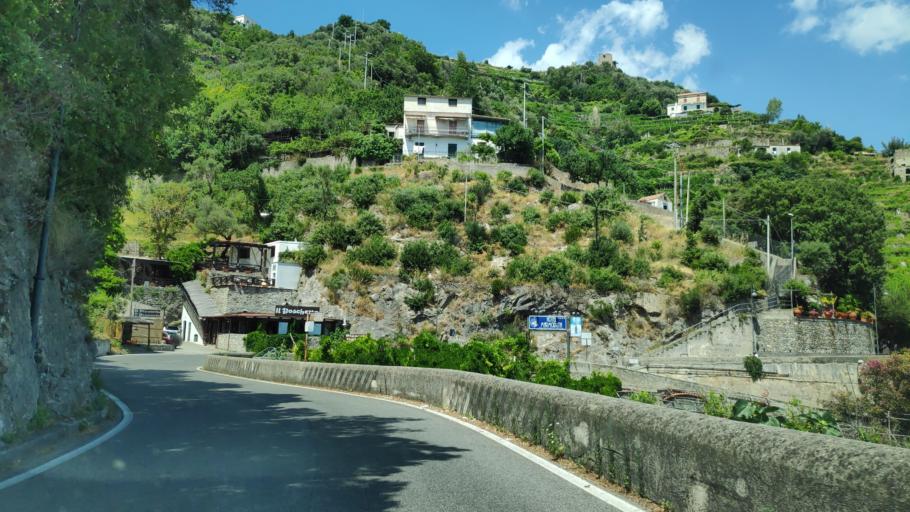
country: IT
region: Campania
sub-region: Provincia di Salerno
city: Ravello
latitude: 40.6456
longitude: 14.6189
